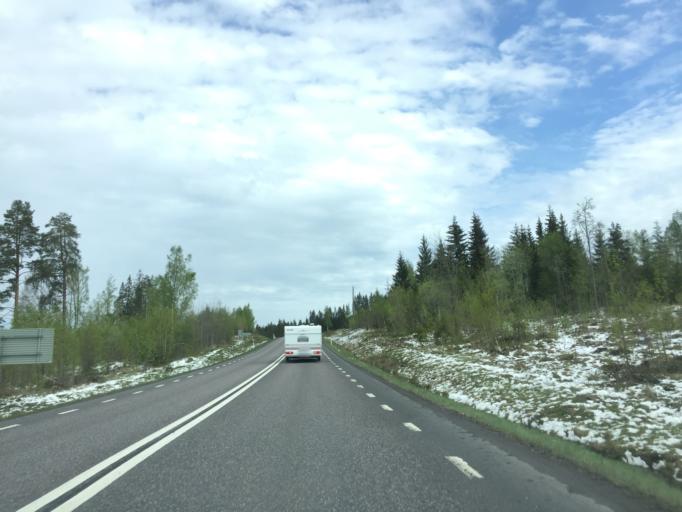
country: SE
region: Dalarna
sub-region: Ludvika Kommun
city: Ludvika
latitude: 60.1064
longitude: 15.1045
